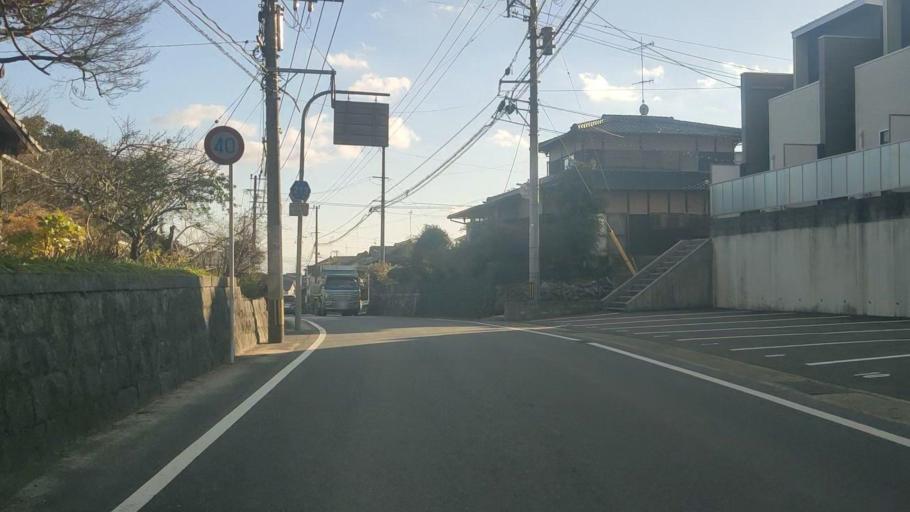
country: JP
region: Saga Prefecture
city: Saga-shi
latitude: 33.3263
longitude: 130.2679
